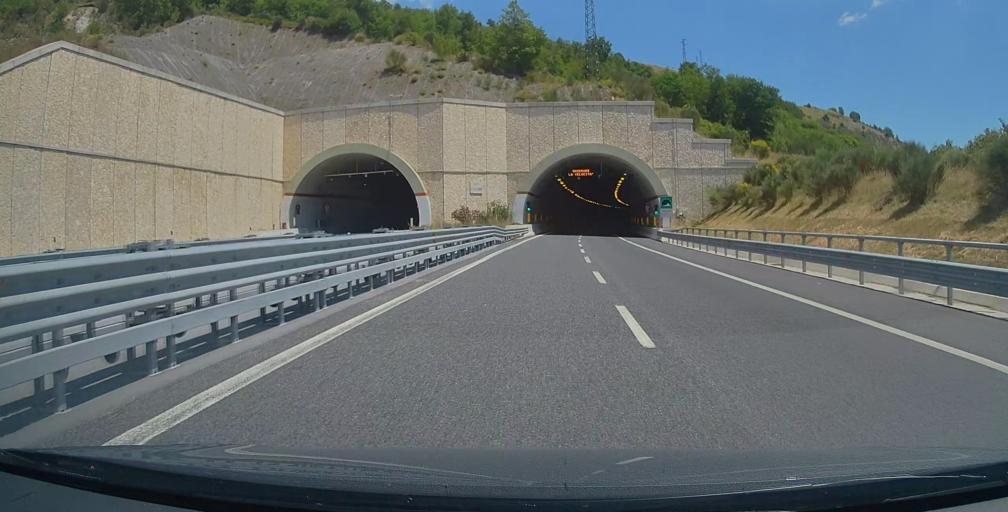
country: IT
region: Calabria
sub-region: Provincia di Cosenza
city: Mormanno
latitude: 39.8894
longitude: 16.0409
